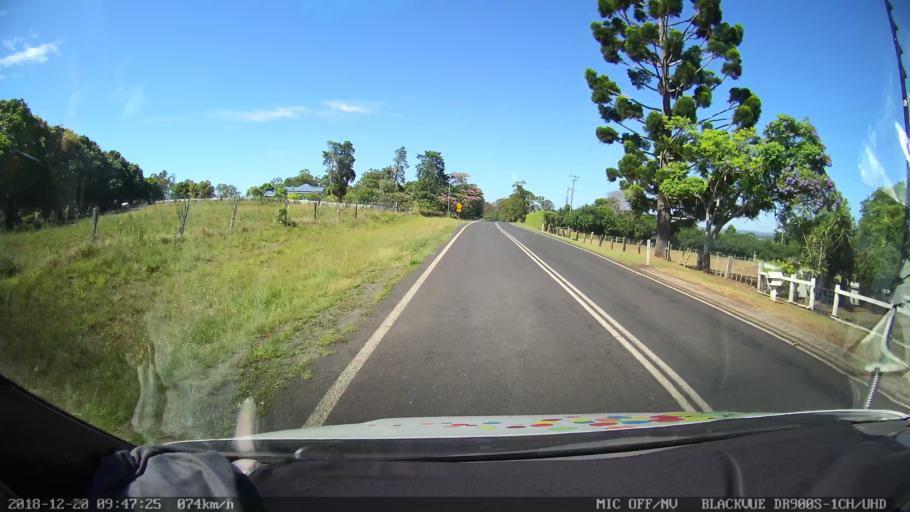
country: AU
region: New South Wales
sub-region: Lismore Municipality
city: Lismore
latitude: -28.7629
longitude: 153.2973
